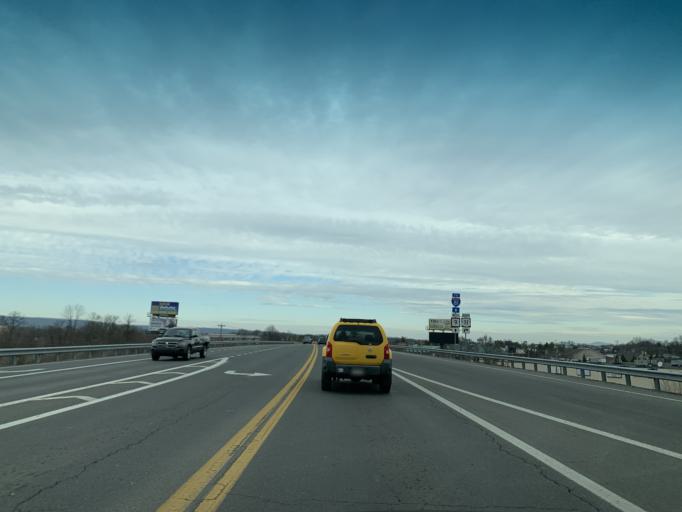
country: US
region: West Virginia
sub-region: Berkeley County
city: Martinsburg
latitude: 39.4728
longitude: -77.9549
